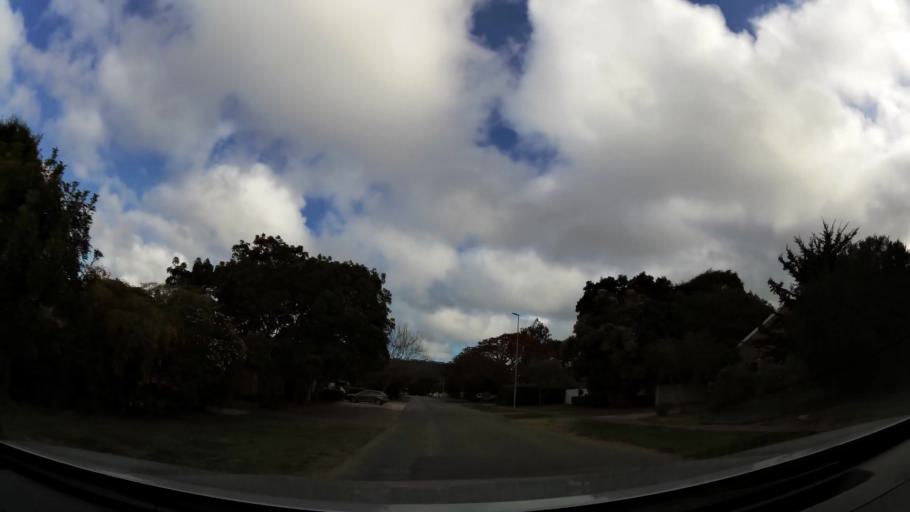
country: ZA
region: Western Cape
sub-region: Eden District Municipality
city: Plettenberg Bay
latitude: -34.0781
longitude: 23.3645
